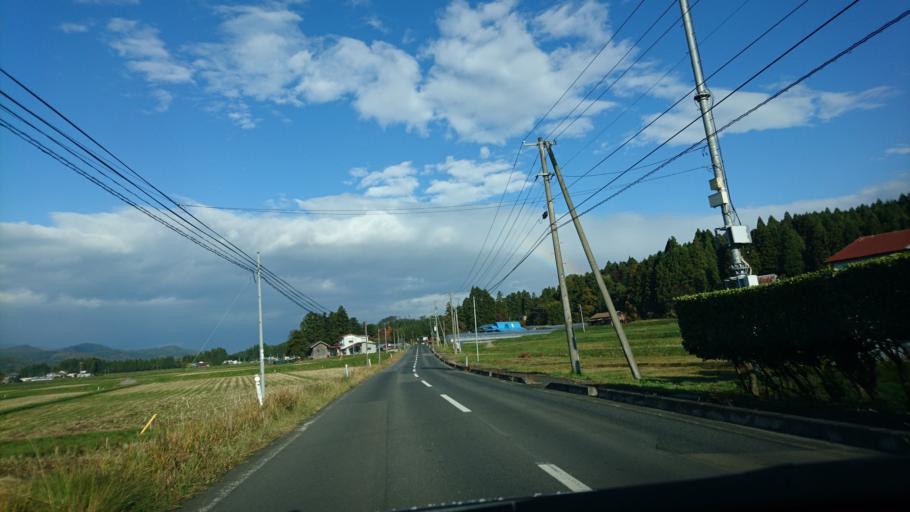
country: JP
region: Iwate
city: Mizusawa
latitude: 39.0295
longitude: 141.0812
